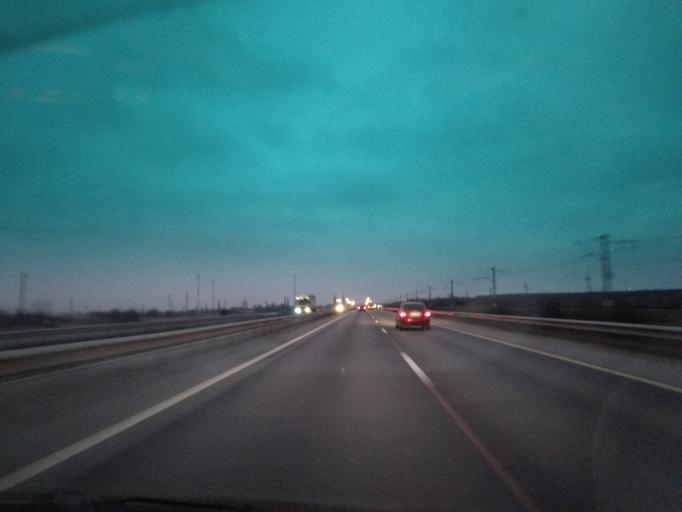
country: RU
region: Adygeya
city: Adygeysk
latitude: 44.8116
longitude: 39.2282
